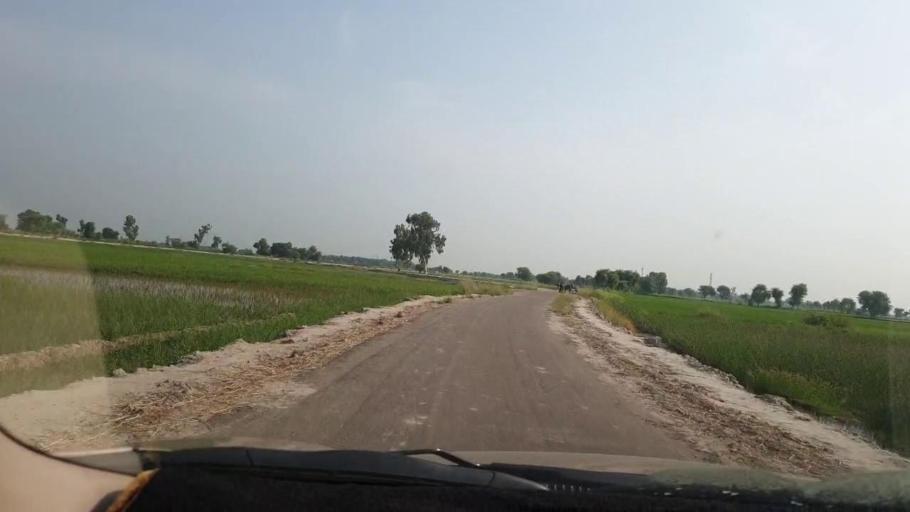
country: PK
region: Sindh
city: Goth Garelo
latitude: 27.4697
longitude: 68.0781
